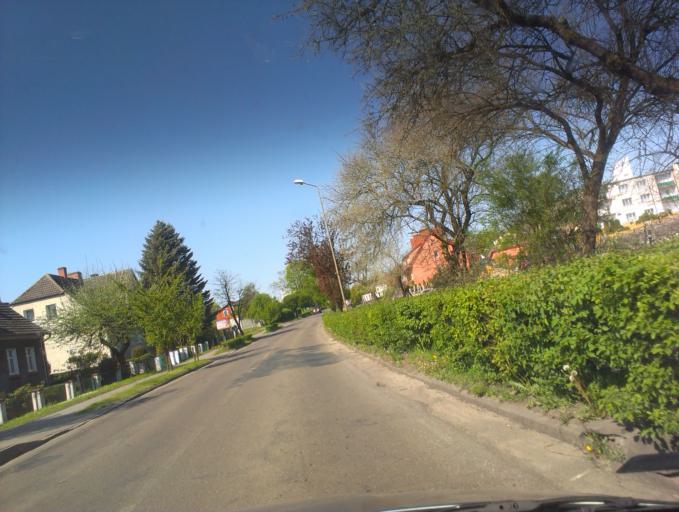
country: PL
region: West Pomeranian Voivodeship
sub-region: Powiat swidwinski
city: Polczyn-Zdroj
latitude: 53.7647
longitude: 16.1066
